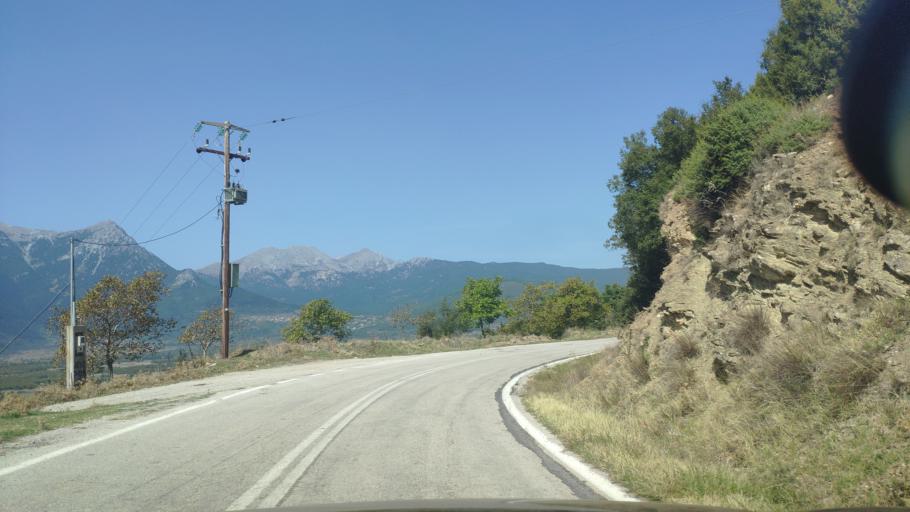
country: GR
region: West Greece
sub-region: Nomos Achaias
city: Aiyira
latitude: 37.8848
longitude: 22.3449
